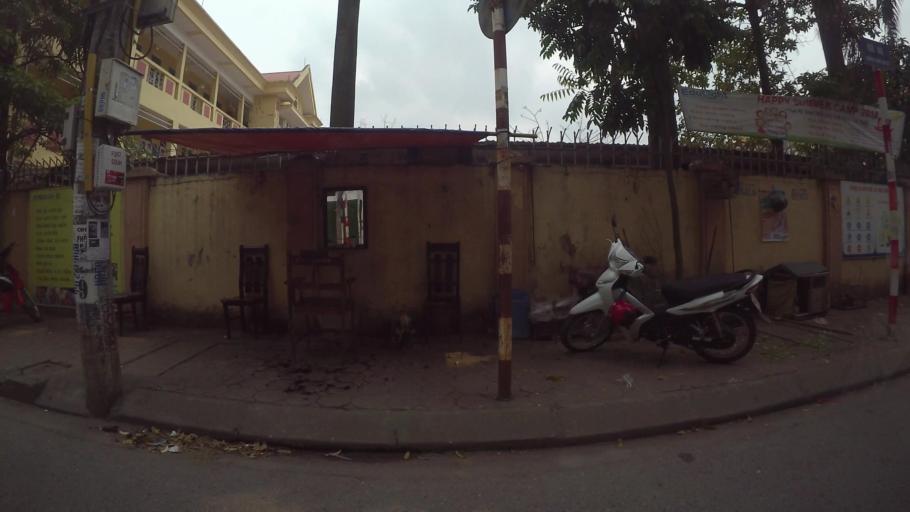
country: VN
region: Ha Noi
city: Trau Quy
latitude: 21.0698
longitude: 105.9063
